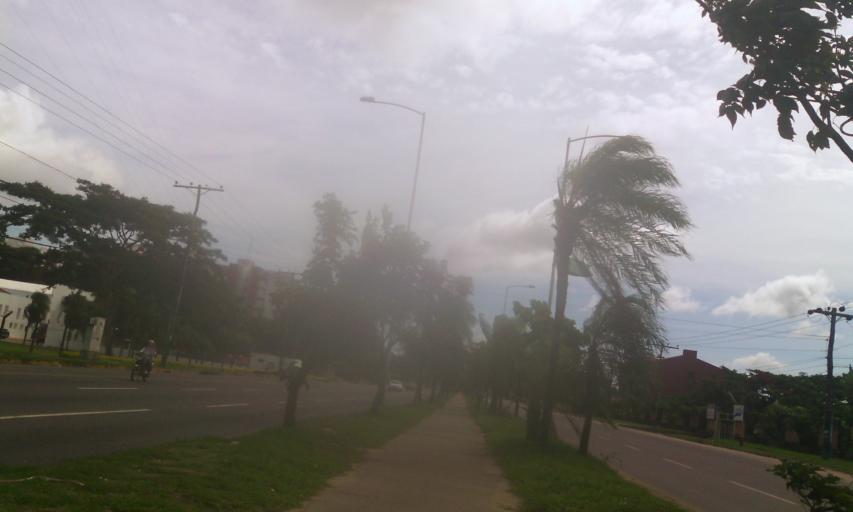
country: BO
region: Santa Cruz
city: Santa Cruz de la Sierra
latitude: -17.8223
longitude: -63.2201
